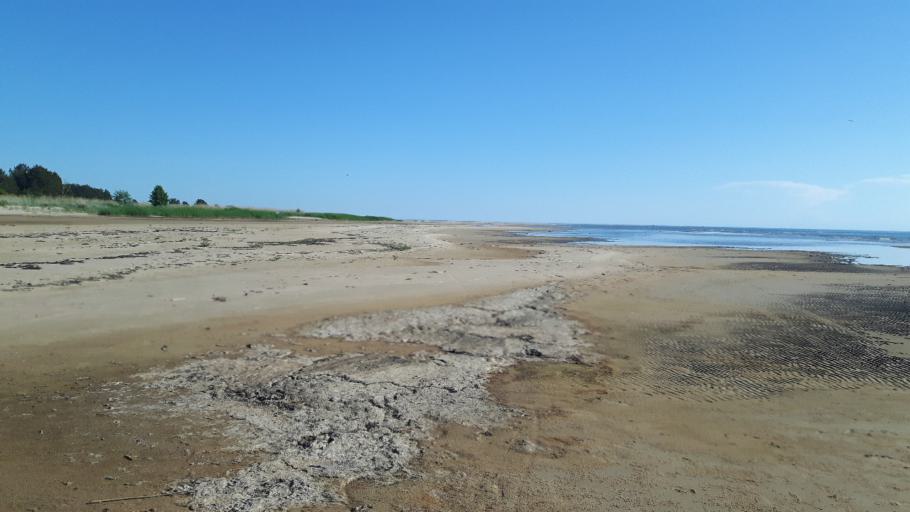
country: LV
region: Salacgrivas
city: Salacgriva
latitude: 57.7065
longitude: 24.3425
